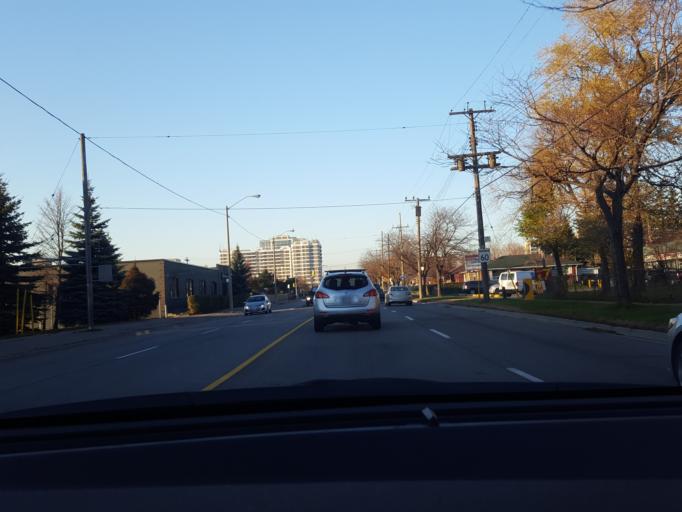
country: CA
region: Ontario
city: Scarborough
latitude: 43.7427
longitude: -79.2829
